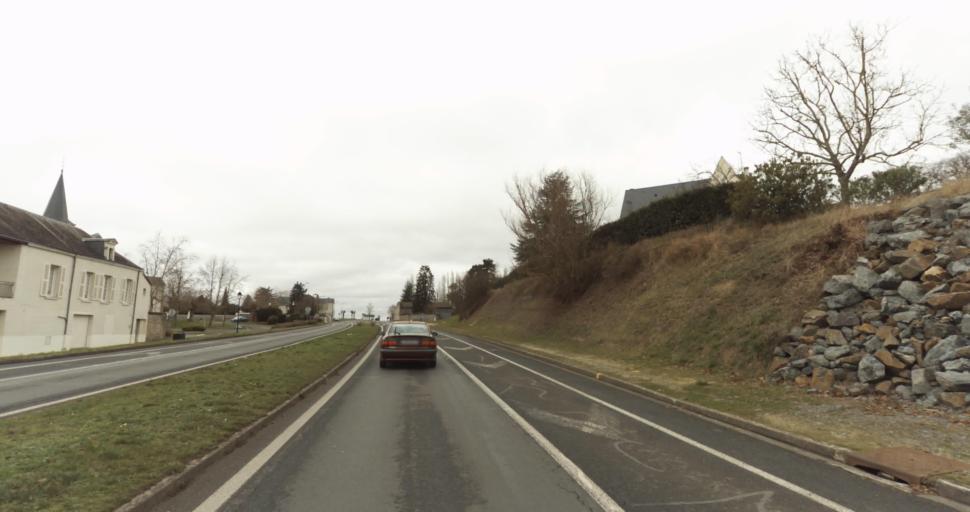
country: FR
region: Pays de la Loire
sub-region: Departement de Maine-et-Loire
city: Varrains
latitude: 47.2260
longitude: -0.0660
